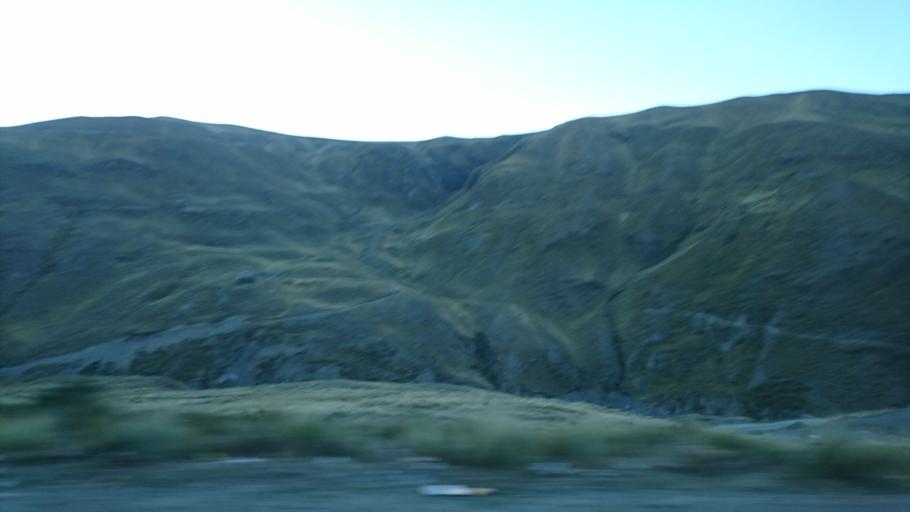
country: BO
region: La Paz
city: La Paz
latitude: -16.4212
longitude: -68.0557
